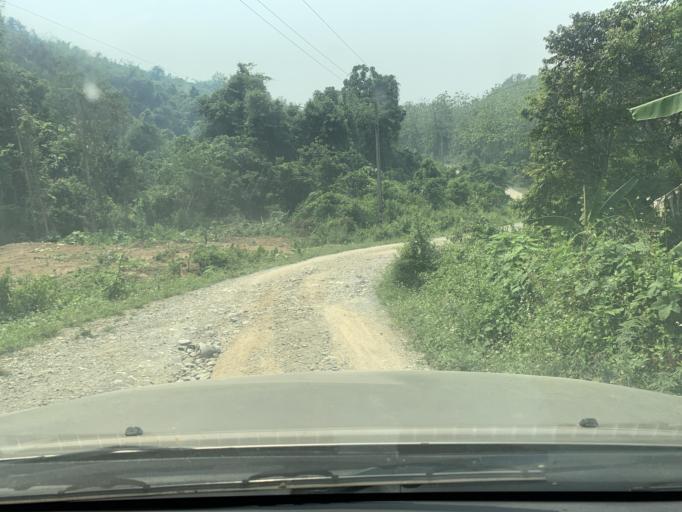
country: LA
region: Louangphabang
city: Louangphabang
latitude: 19.8819
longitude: 102.2619
